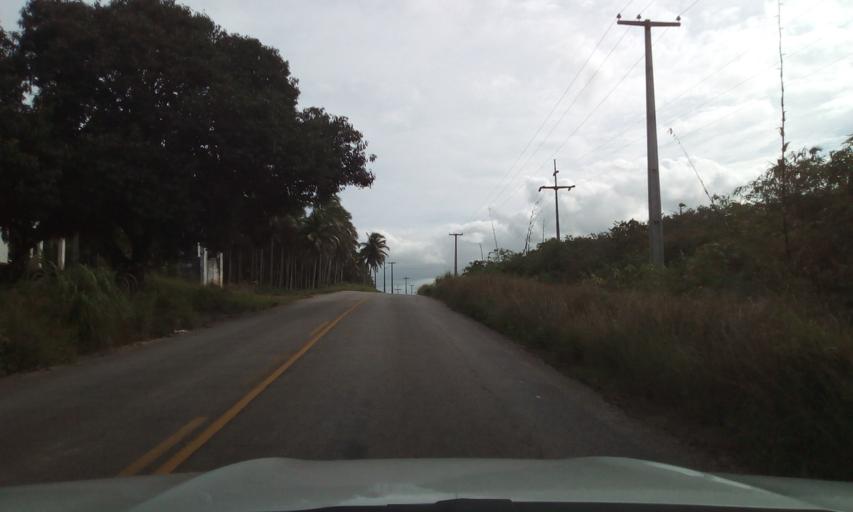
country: BR
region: Paraiba
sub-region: Cabedelo
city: Cabedelo
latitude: -6.9462
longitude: -34.9307
